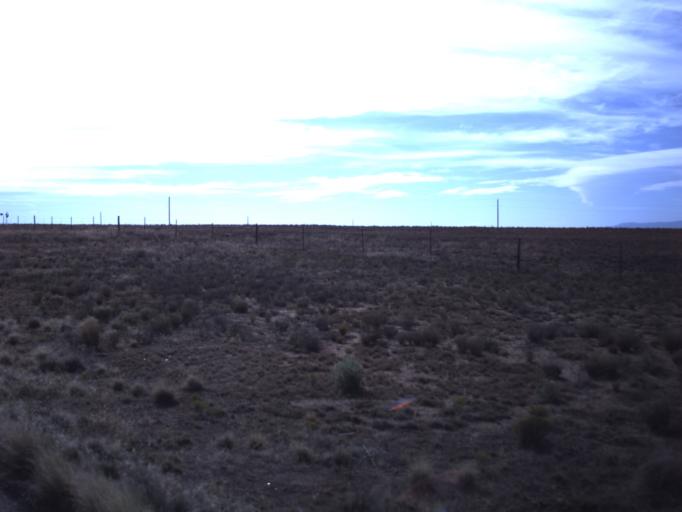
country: US
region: Utah
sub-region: San Juan County
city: Blanding
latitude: 37.4339
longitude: -109.3733
